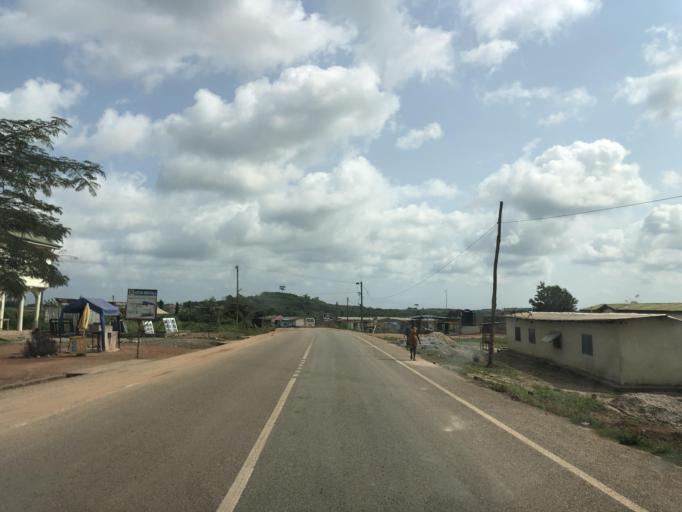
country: GH
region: Central
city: Elmina
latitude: 5.1963
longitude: -1.3200
